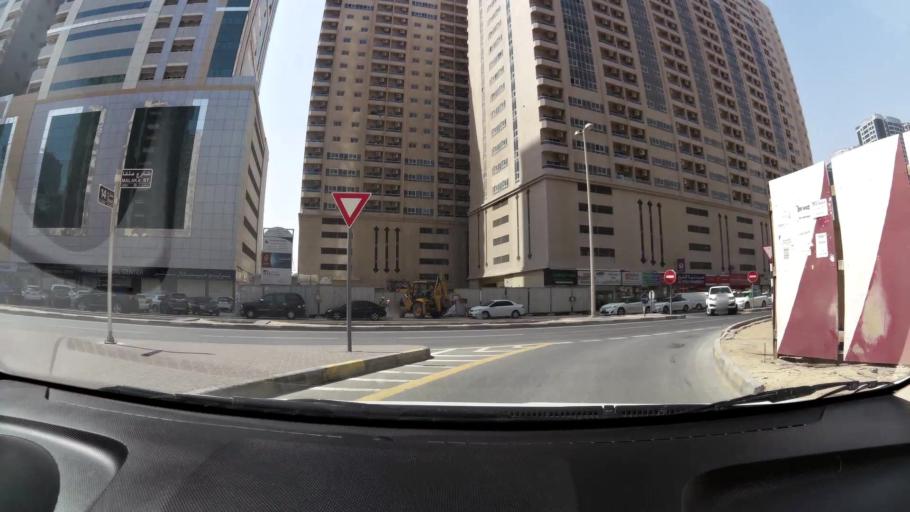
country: AE
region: Ash Shariqah
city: Sharjah
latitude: 25.3005
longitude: 55.3703
